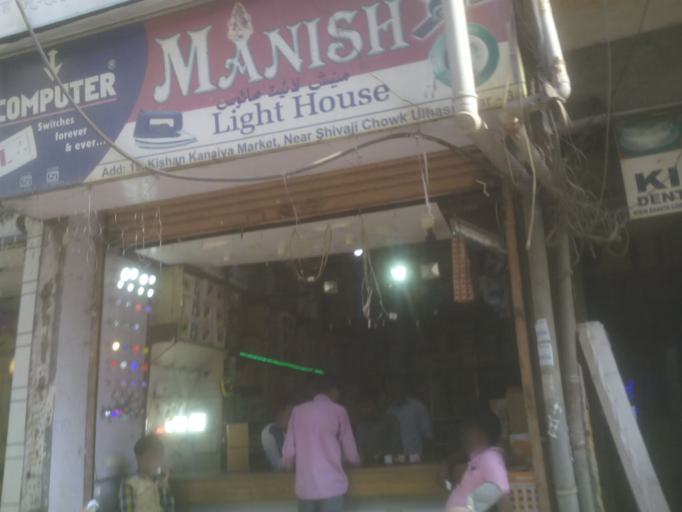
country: IN
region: Maharashtra
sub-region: Thane
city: Ulhasnagar
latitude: 19.2267
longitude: 73.1612
